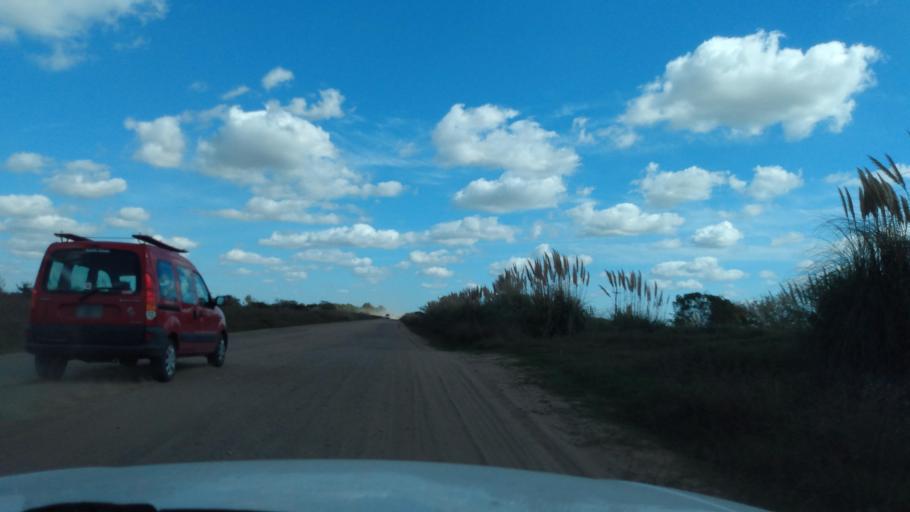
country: AR
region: Buenos Aires
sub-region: Partido de Navarro
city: Navarro
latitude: -35.0047
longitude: -59.3734
